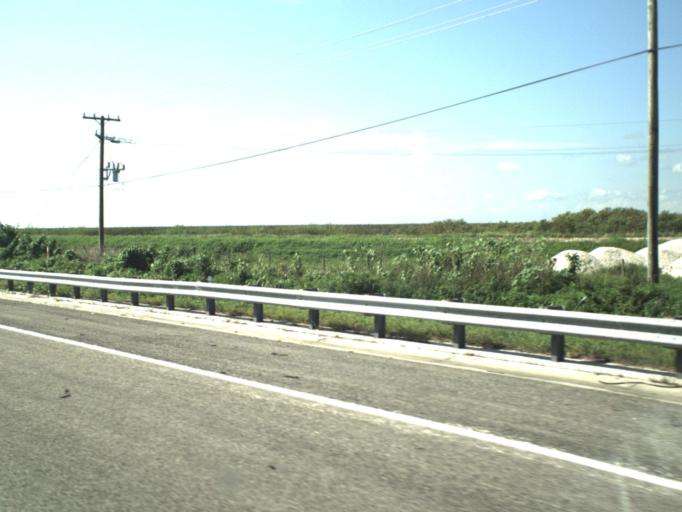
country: US
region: Florida
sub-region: Palm Beach County
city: Belle Glade Camp
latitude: 26.3964
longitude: -80.5856
